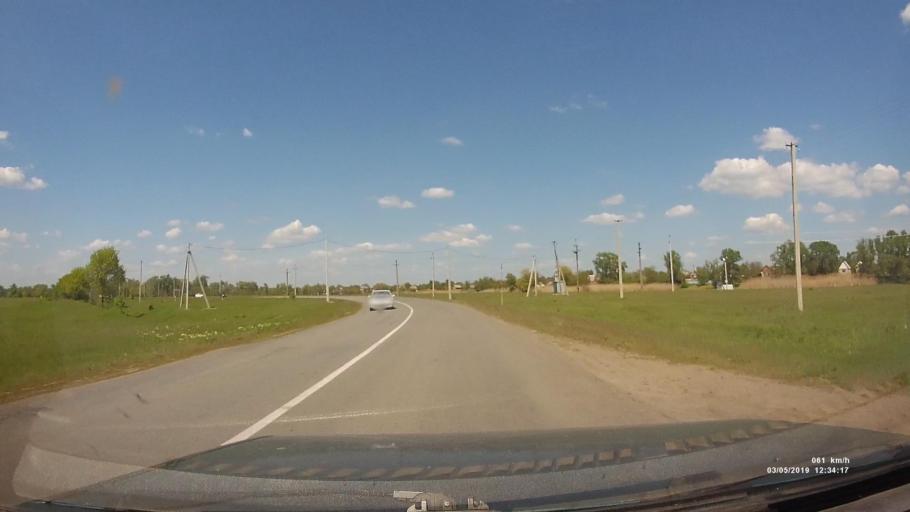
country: RU
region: Rostov
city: Semikarakorsk
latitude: 47.5211
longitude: 40.7687
